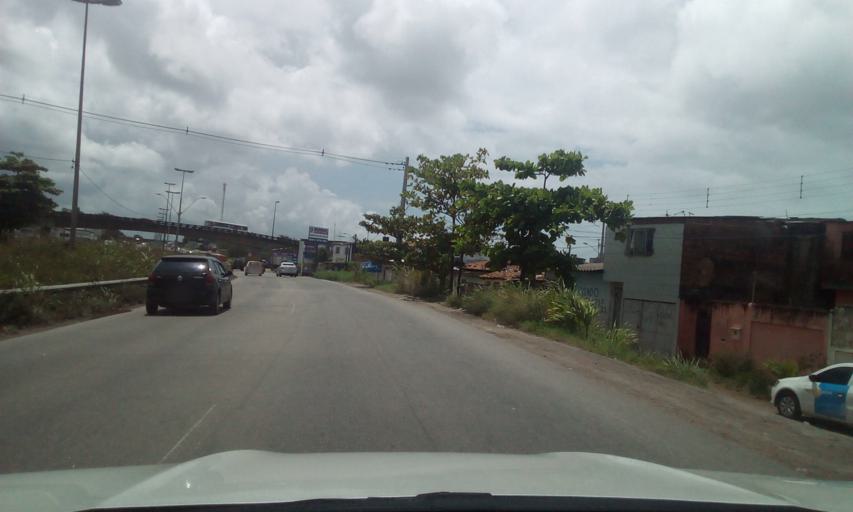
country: BR
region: Pernambuco
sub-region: Recife
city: Recife
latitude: -8.0827
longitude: -34.9434
